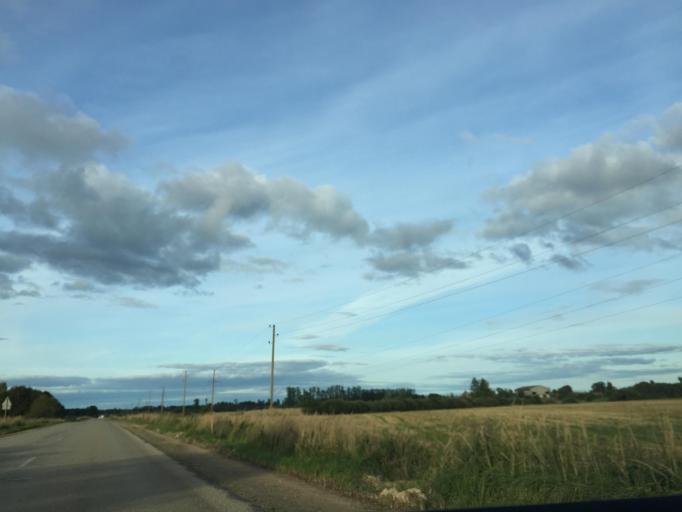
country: LV
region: Nereta
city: Nereta
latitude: 56.2671
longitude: 25.3682
